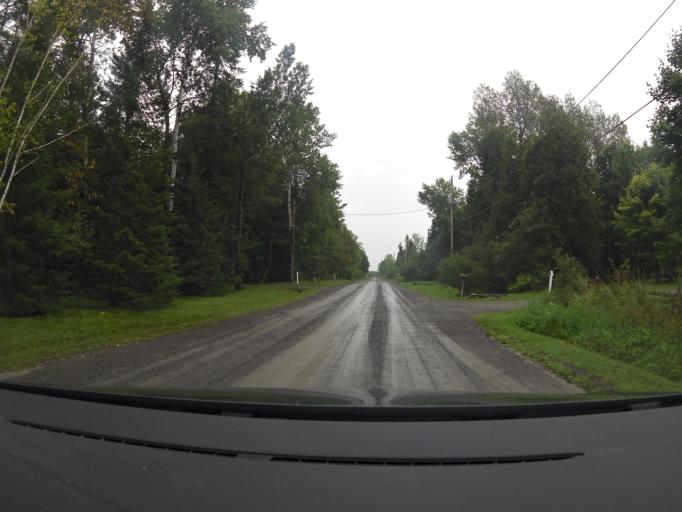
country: CA
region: Ontario
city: Carleton Place
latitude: 45.1797
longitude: -76.0722
